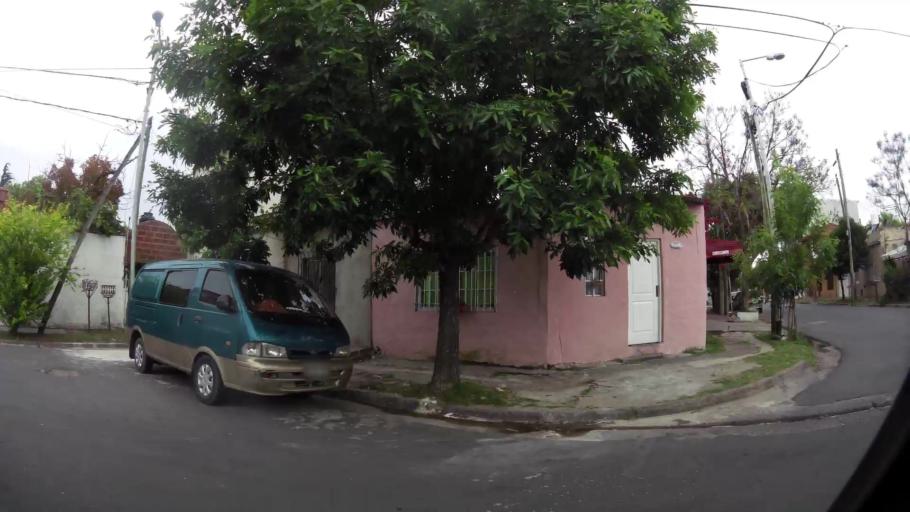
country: AR
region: Buenos Aires
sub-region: Partido de Avellaneda
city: Avellaneda
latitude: -34.6742
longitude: -58.3468
